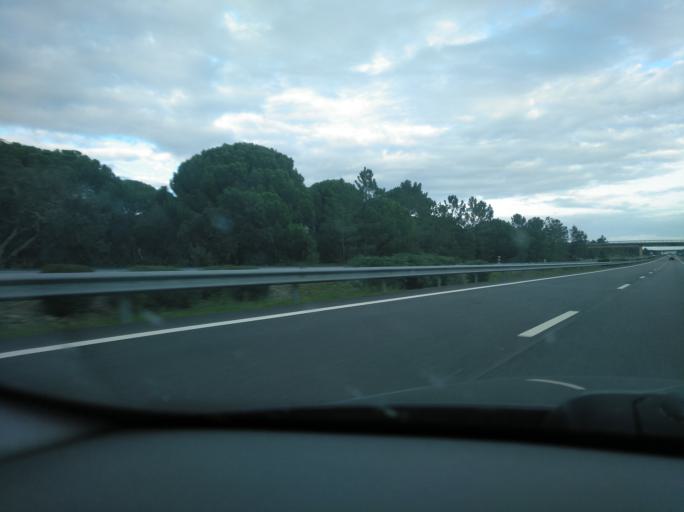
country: PT
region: Evora
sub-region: Vendas Novas
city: Vendas Novas
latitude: 38.6116
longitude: -8.6217
